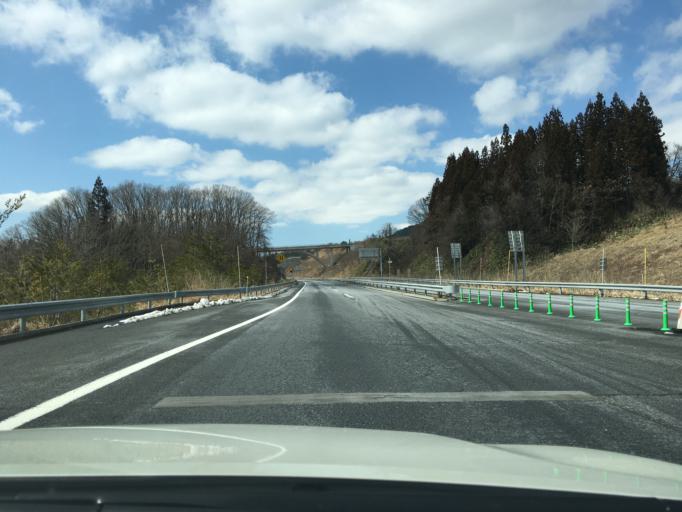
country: JP
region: Yamagata
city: Sagae
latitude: 38.4249
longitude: 140.1625
